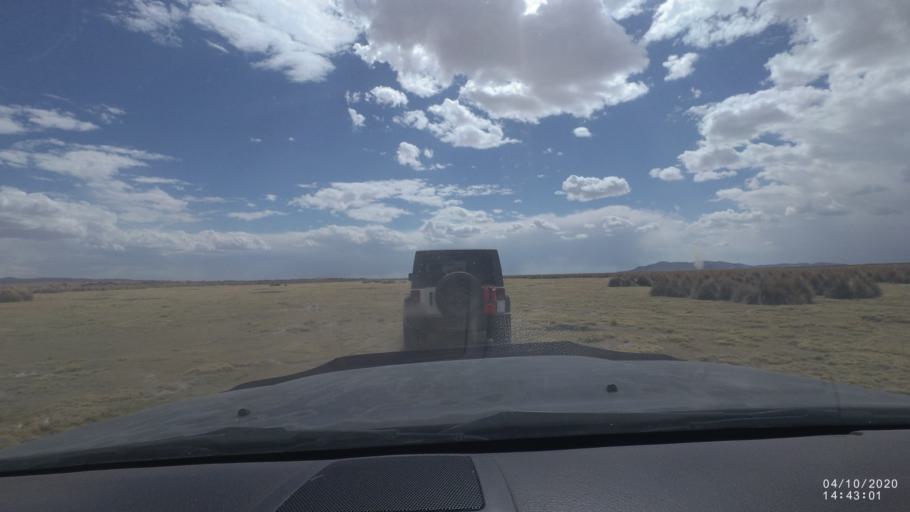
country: BO
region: Oruro
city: Poopo
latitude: -18.6867
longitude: -67.4923
